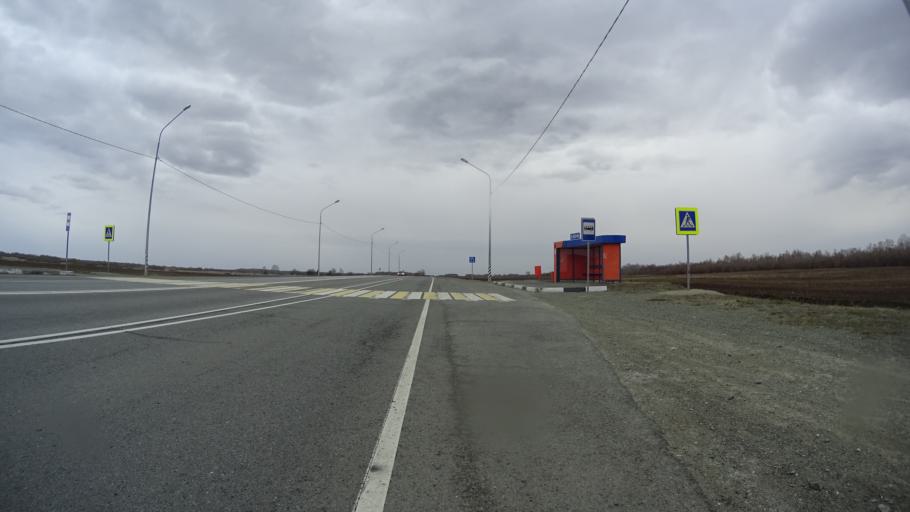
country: RU
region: Chelyabinsk
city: Krasnogorskiy
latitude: 54.6721
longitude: 61.2499
